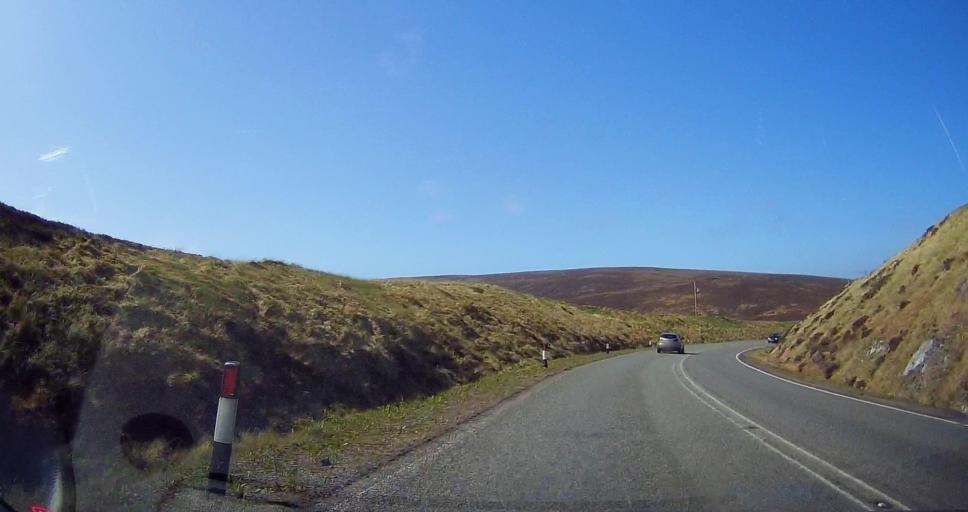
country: GB
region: Scotland
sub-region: Shetland Islands
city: Lerwick
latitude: 60.1373
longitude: -1.2277
